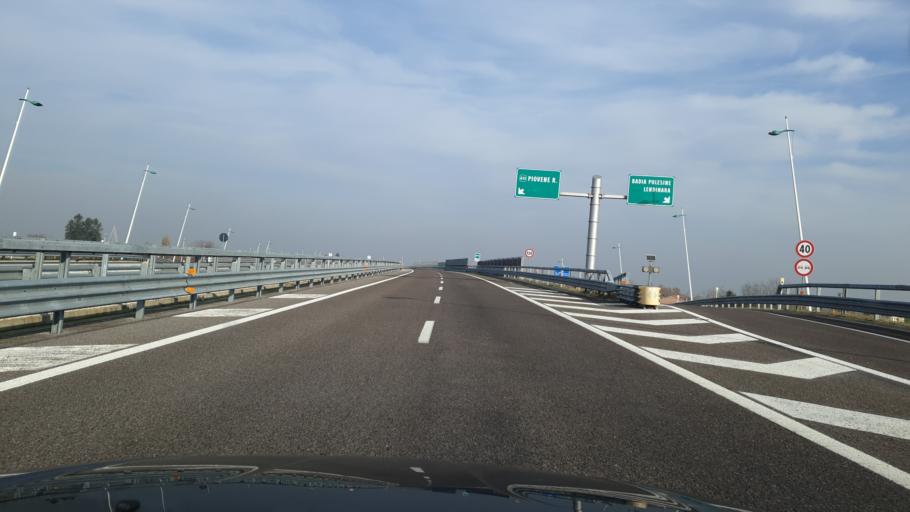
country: IT
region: Veneto
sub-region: Provincia di Rovigo
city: Badia Polesine
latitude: 45.0900
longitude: 11.5260
